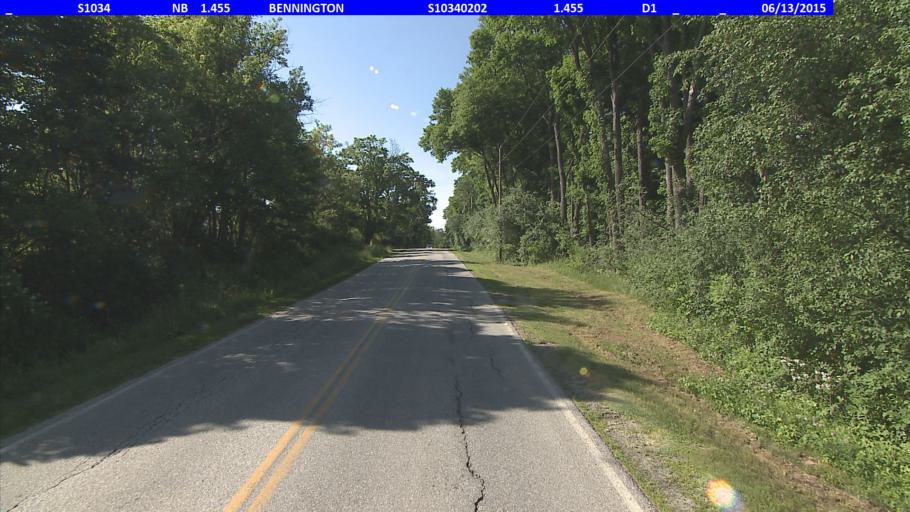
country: US
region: Vermont
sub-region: Bennington County
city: Bennington
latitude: 42.8715
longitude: -73.2117
